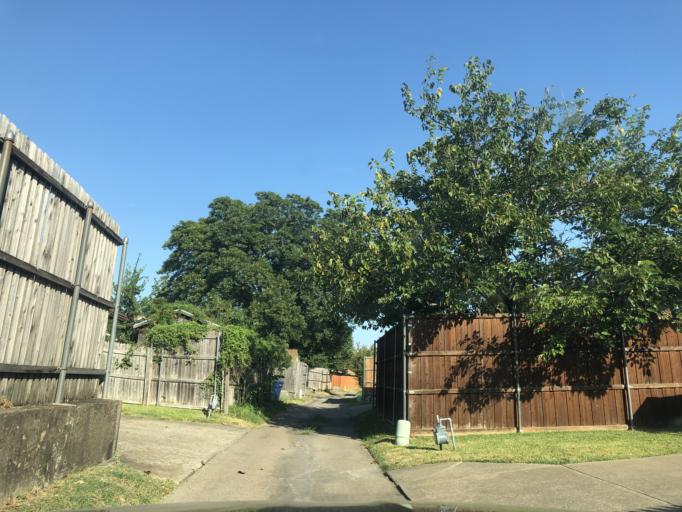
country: US
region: Texas
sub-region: Dallas County
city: Garland
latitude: 32.8556
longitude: -96.6296
